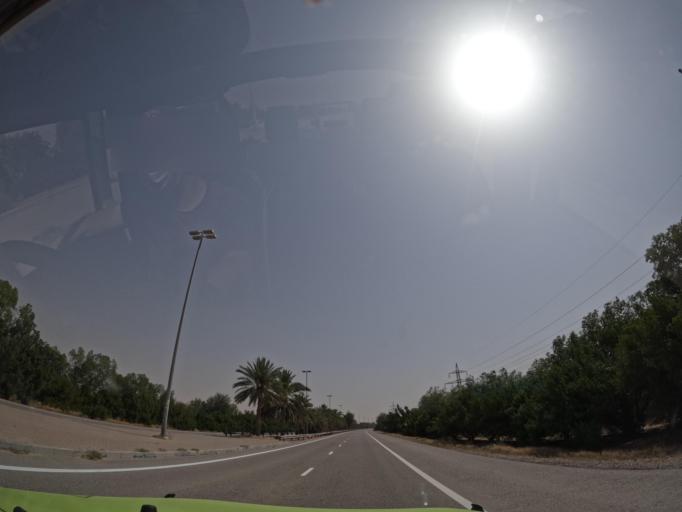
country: OM
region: Al Buraimi
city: Al Buraymi
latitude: 24.6764
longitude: 55.6927
